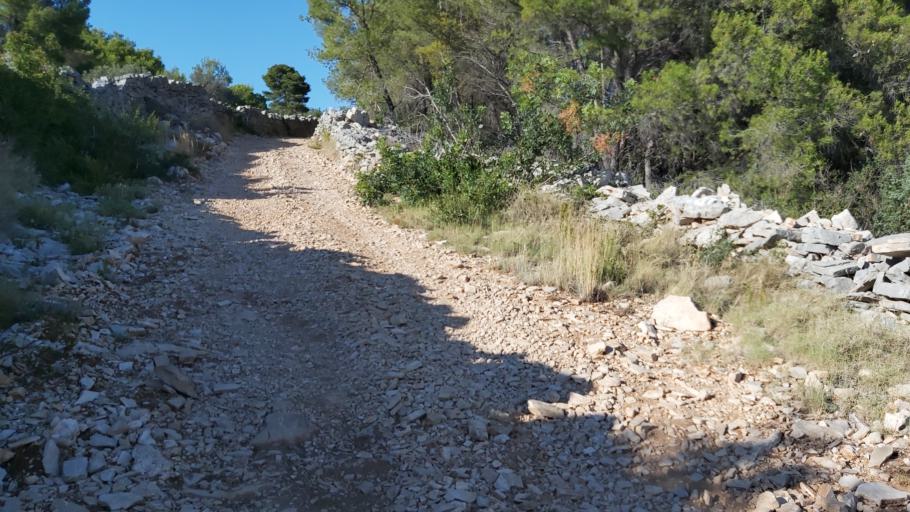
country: HR
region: Splitsko-Dalmatinska
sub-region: Grad Trogir
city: Trogir
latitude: 43.3750
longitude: 16.2872
